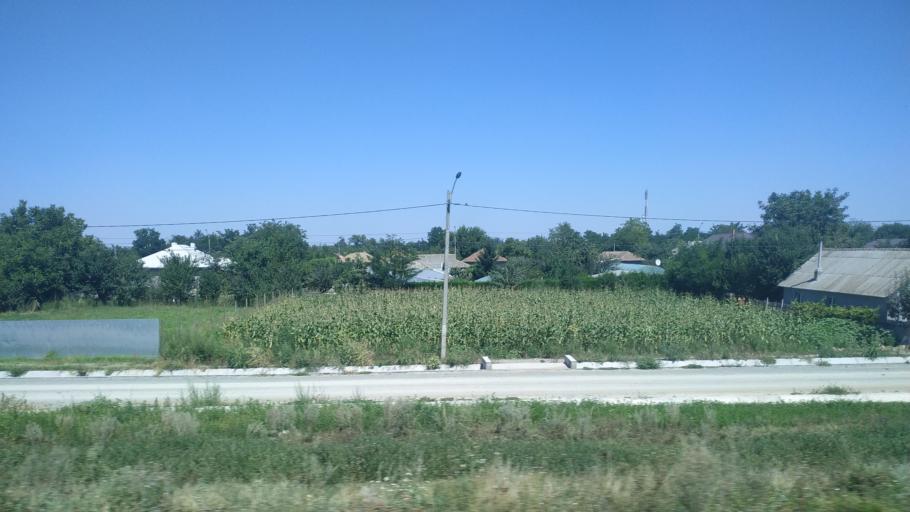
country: RO
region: Calarasi
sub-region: Comuna Perisoru
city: Perisoru
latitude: 44.4216
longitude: 27.6346
